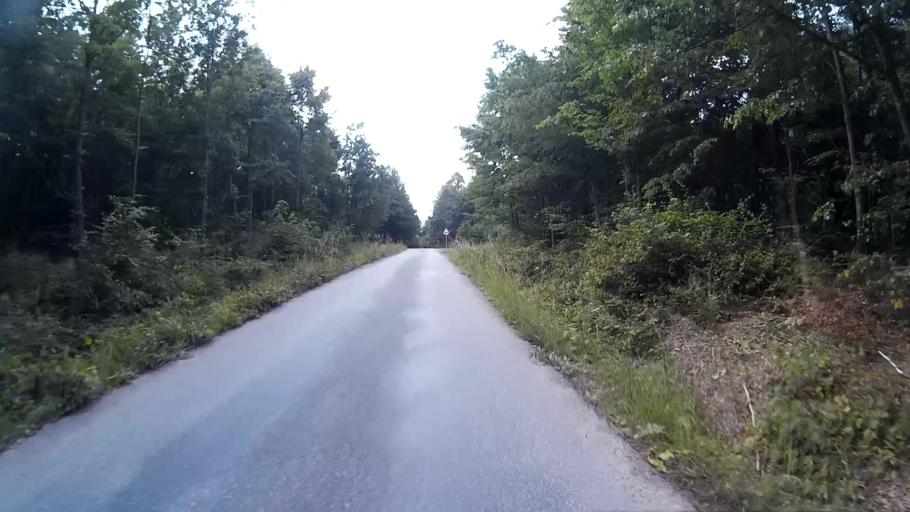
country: CZ
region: South Moravian
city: Veverska Bityska
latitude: 49.2217
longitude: 16.4543
